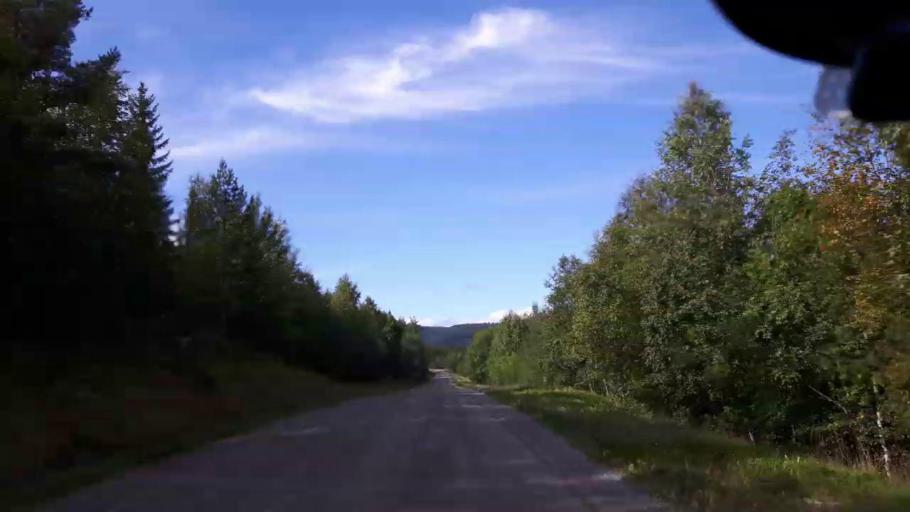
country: SE
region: Jaemtland
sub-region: Ragunda Kommun
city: Hammarstrand
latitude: 63.1339
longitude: 16.1148
